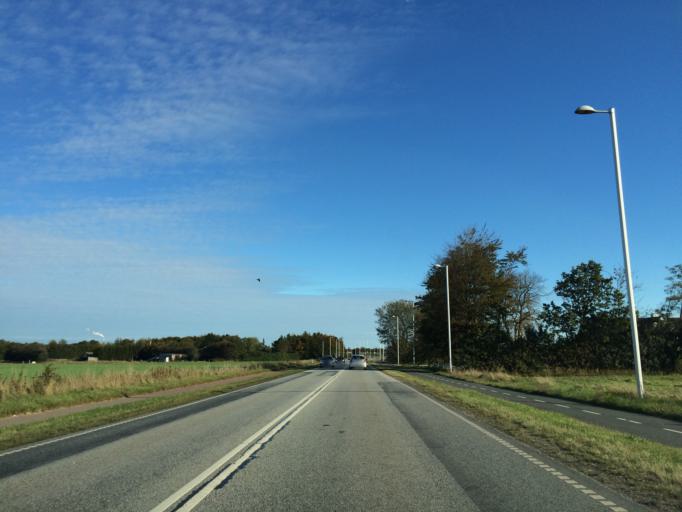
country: DK
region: Central Jutland
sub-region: Randers Kommune
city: Randers
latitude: 56.4249
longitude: 10.0292
